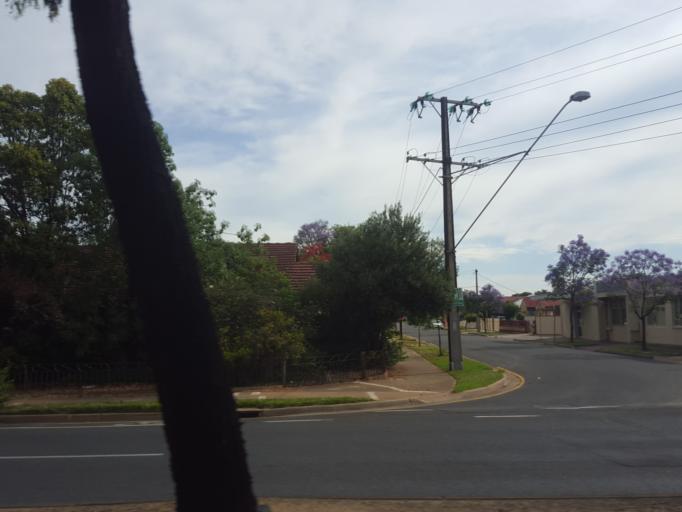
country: AU
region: South Australia
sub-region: Charles Sturt
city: Woodville
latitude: -34.8838
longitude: 138.5627
